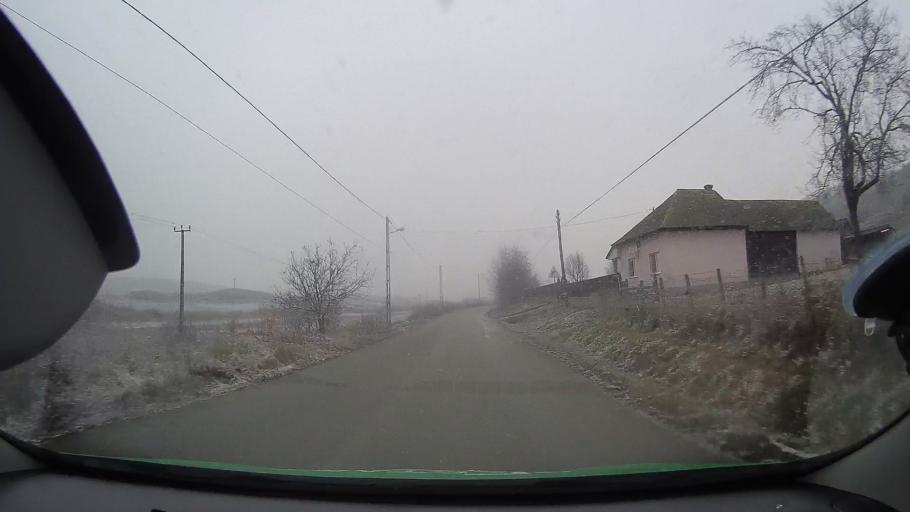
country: RO
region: Alba
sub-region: Comuna Noslac
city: Noslac
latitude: 46.3402
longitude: 23.9487
